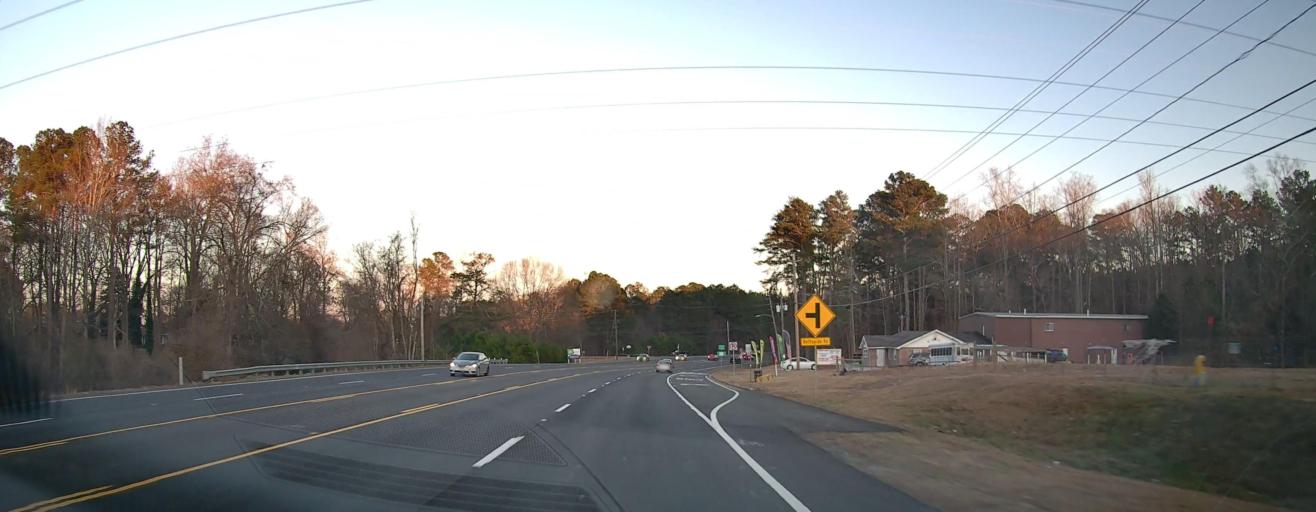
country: US
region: Georgia
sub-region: Fulton County
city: Union City
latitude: 33.5593
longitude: -84.5089
